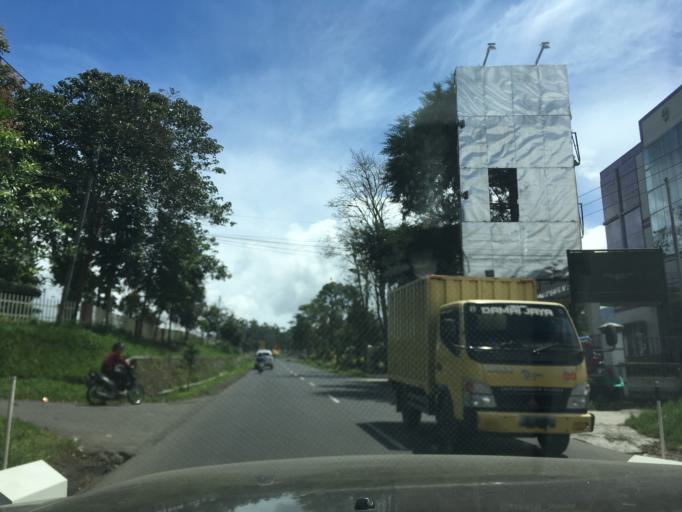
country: ID
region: West Java
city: Lembang
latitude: -6.8020
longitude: 107.6503
